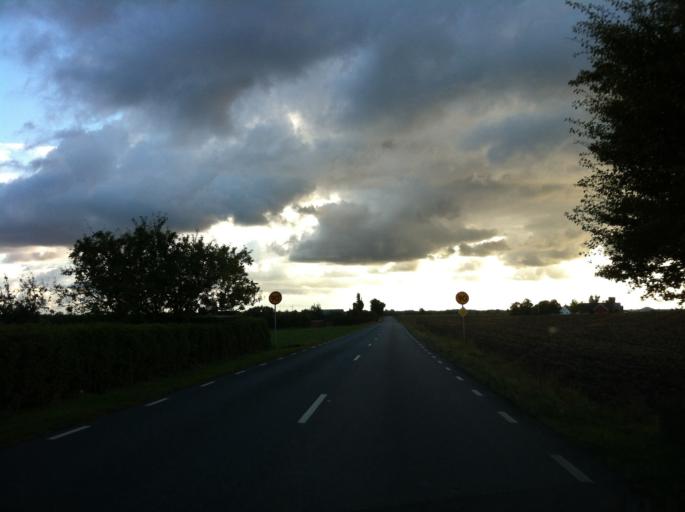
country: SE
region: Skane
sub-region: Svalovs Kommun
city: Svaloev
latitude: 55.8911
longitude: 13.1791
